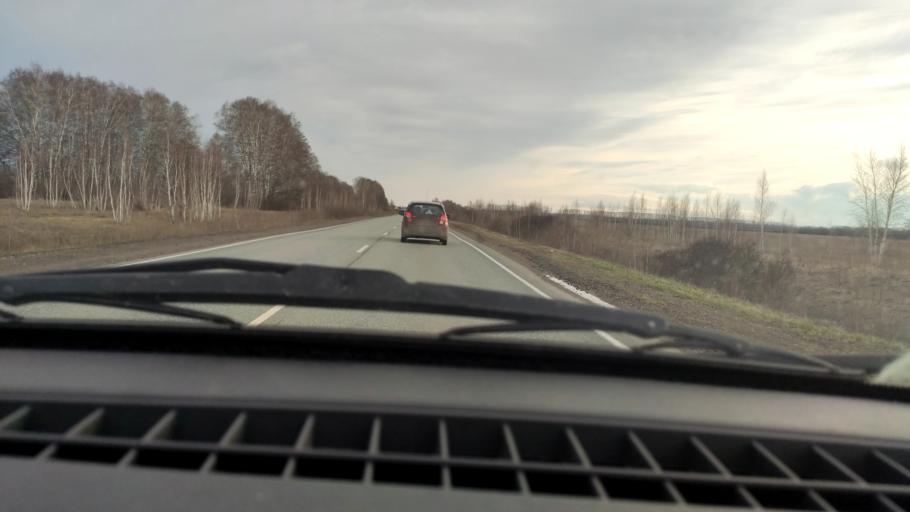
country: RU
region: Bashkortostan
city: Chishmy
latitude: 54.4193
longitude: 55.2272
